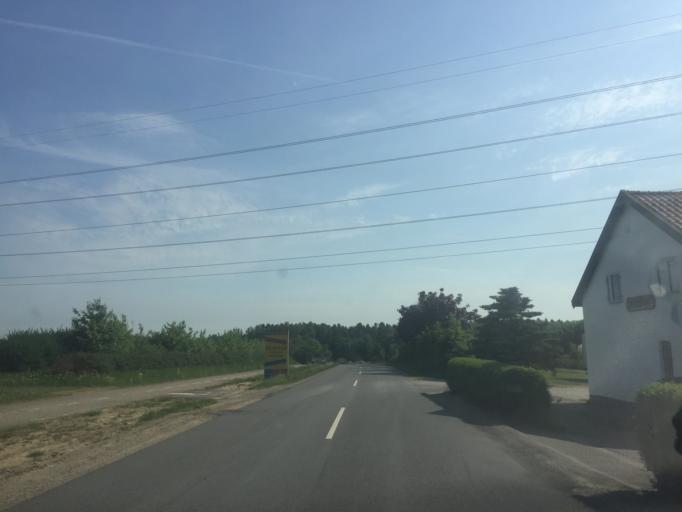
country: DK
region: Capital Region
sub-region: Egedal Kommune
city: Smorumnedre
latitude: 55.7273
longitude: 12.2907
